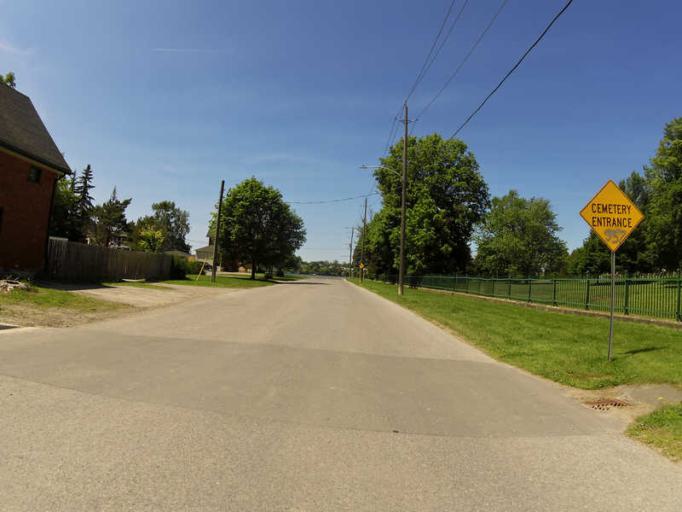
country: CA
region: Ontario
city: Peterborough
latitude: 44.2925
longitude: -78.3104
